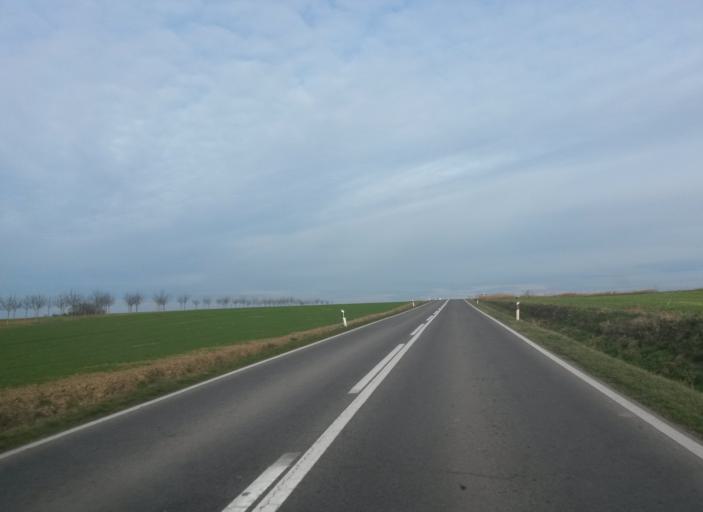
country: HR
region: Osjecko-Baranjska
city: Viskovci
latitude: 45.3722
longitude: 18.4365
